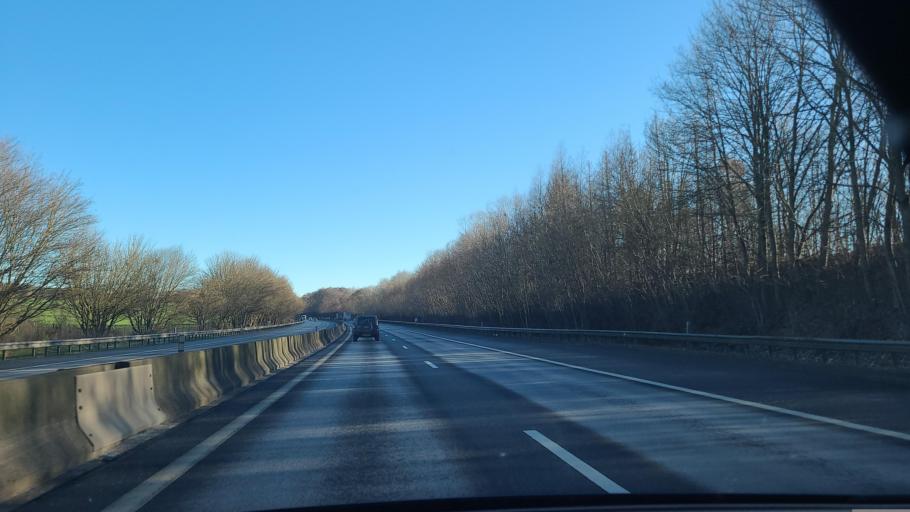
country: LU
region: Luxembourg
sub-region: Canton de Capellen
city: Mamer
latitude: 49.6332
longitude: 6.0344
